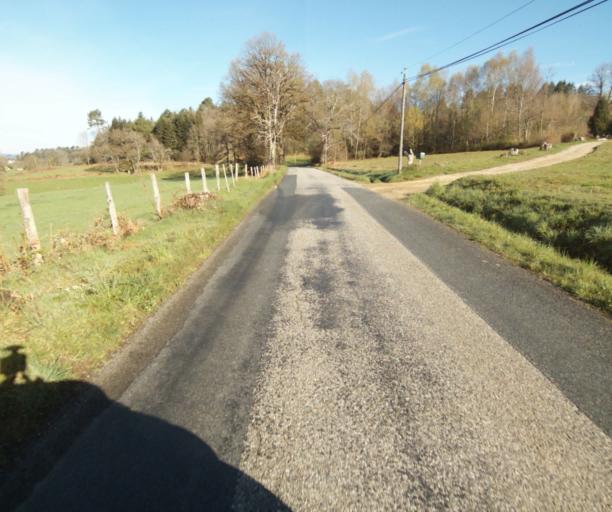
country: FR
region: Limousin
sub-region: Departement de la Correze
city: Laguenne
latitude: 45.2736
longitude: 1.8639
